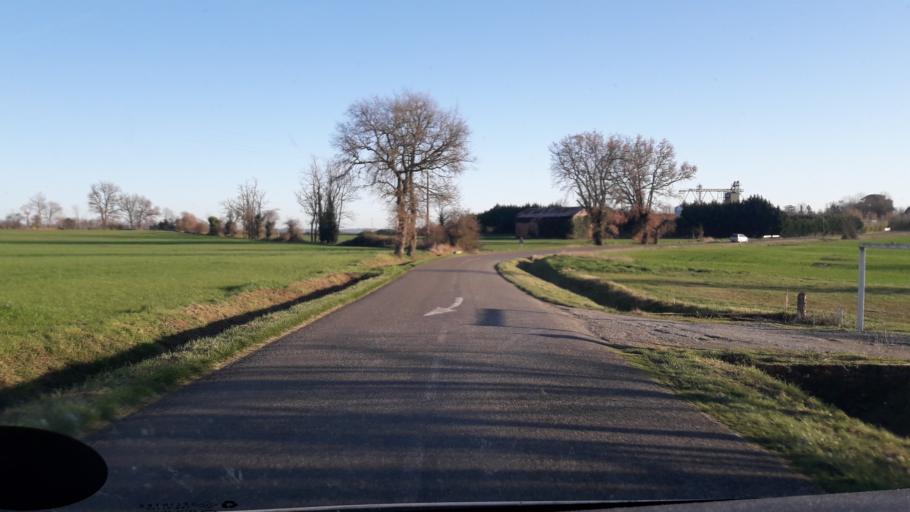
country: FR
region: Midi-Pyrenees
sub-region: Departement du Gers
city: Gimont
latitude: 43.6057
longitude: 0.9786
